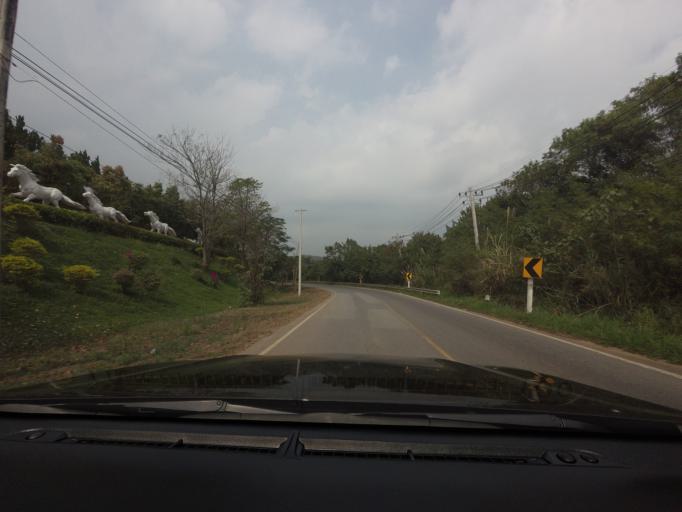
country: TH
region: Nakhon Ratchasima
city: Pak Chong
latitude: 14.4976
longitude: 101.5538
